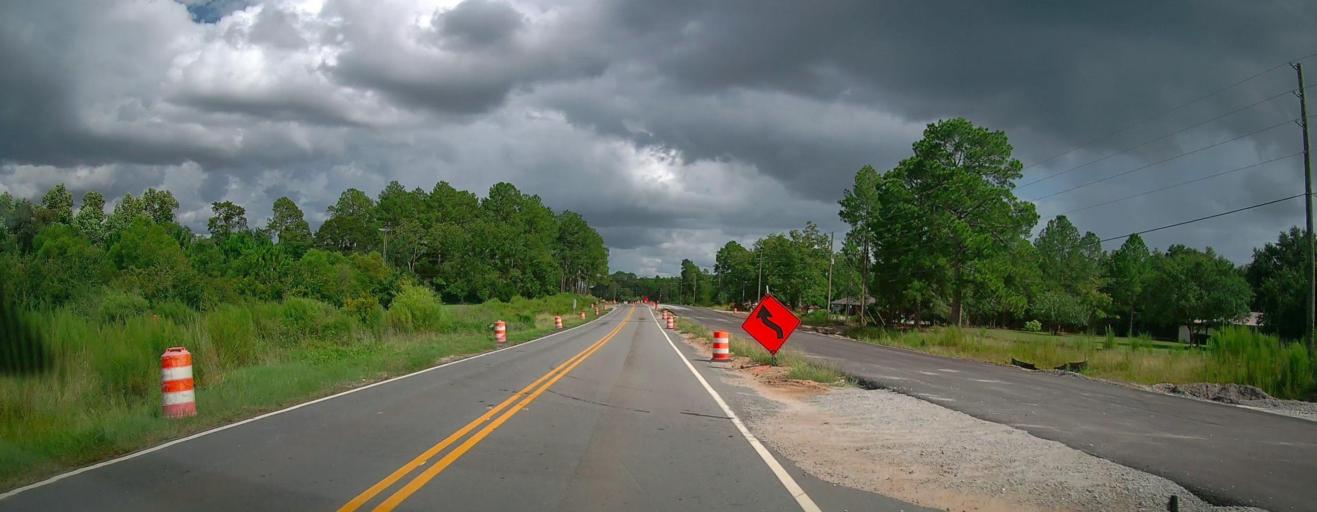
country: US
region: Georgia
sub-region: Coffee County
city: Douglas
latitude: 31.5296
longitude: -82.9096
